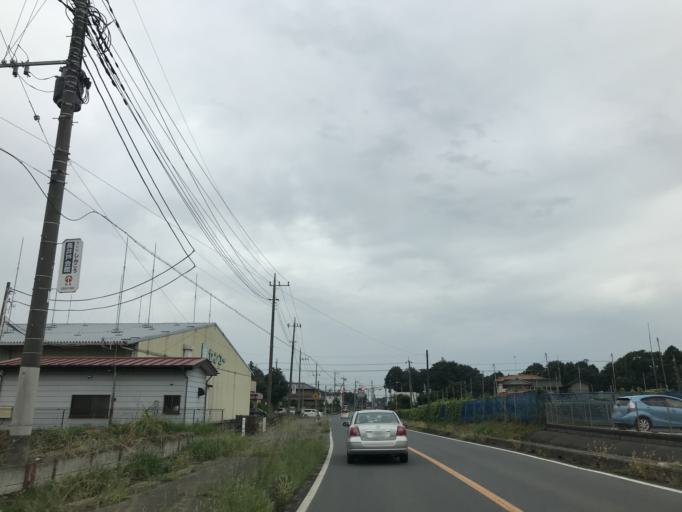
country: JP
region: Ibaraki
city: Sakai
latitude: 36.1254
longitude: 139.7926
